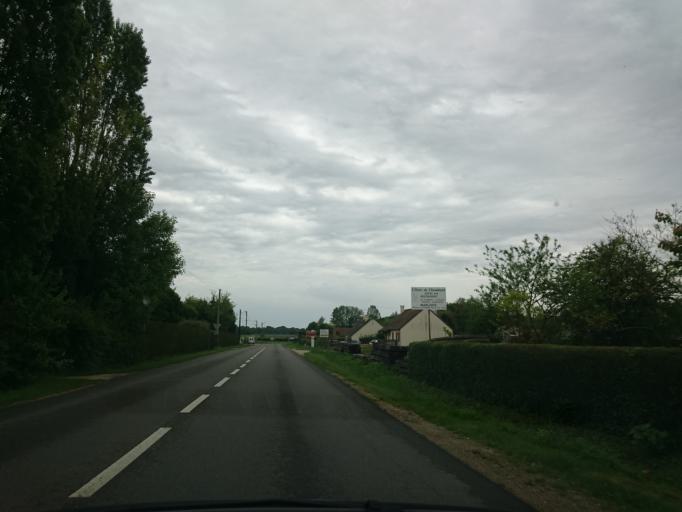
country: FR
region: Centre
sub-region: Departement du Loir-et-Cher
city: Muides-sur-Loire
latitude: 47.6693
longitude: 1.5313
